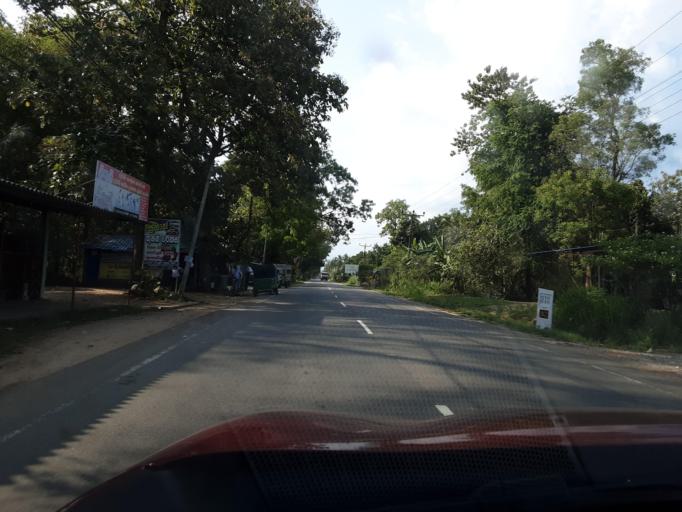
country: LK
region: Uva
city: Haputale
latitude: 6.6586
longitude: 81.1149
